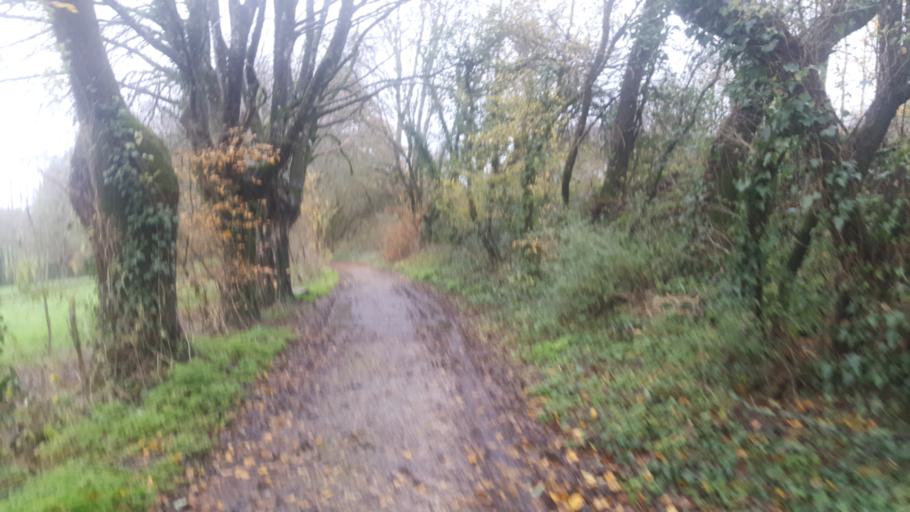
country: FR
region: Poitou-Charentes
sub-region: Departement des Deux-Sevres
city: Melle
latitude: 46.2295
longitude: -0.1484
